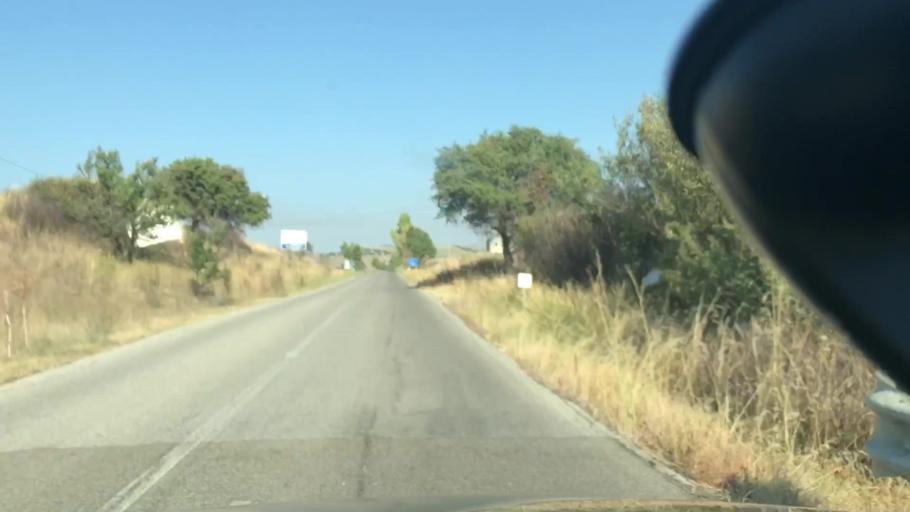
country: IT
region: Basilicate
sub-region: Provincia di Matera
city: La Martella
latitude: 40.6666
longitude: 16.4897
